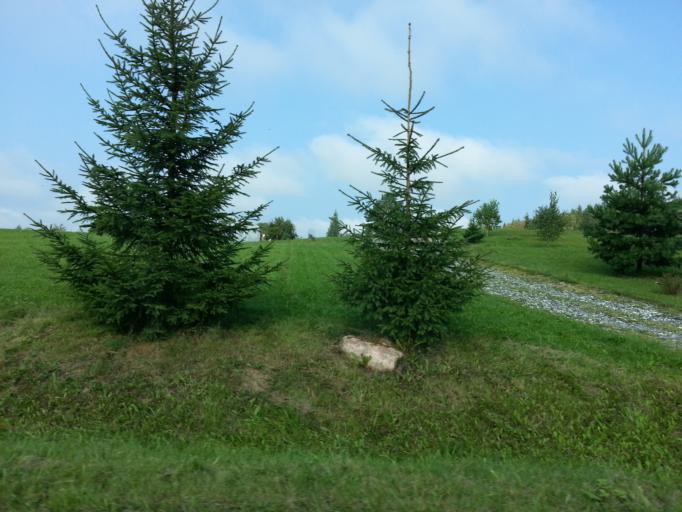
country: LT
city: Grigiskes
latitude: 54.7697
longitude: 25.0533
